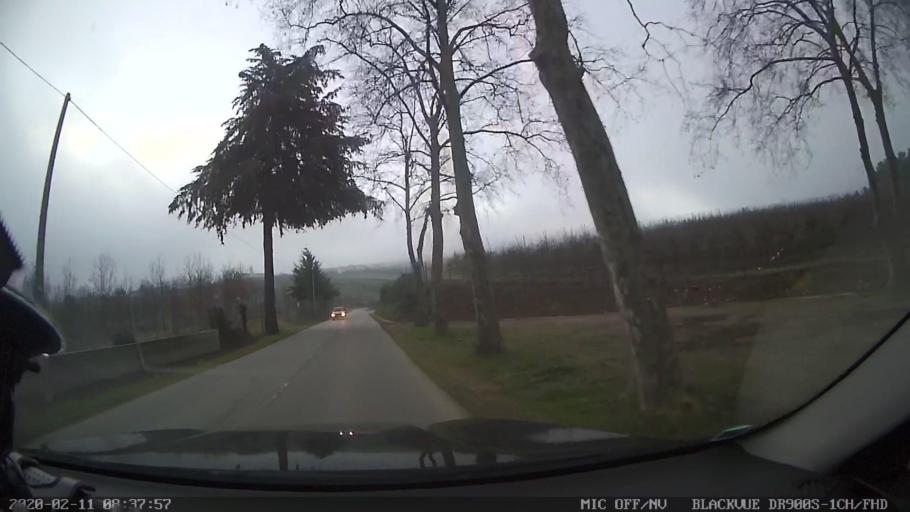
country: PT
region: Vila Real
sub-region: Sabrosa
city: Sabrosa
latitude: 41.2525
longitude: -7.5855
